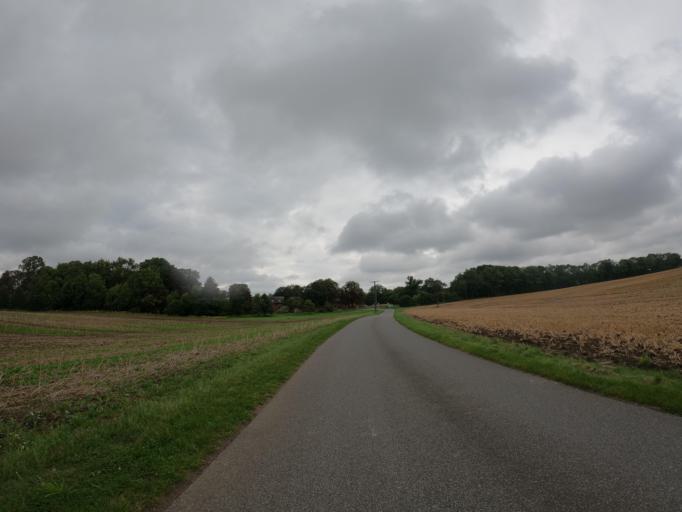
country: DE
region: Mecklenburg-Vorpommern
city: Poseritz
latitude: 54.2891
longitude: 13.3131
